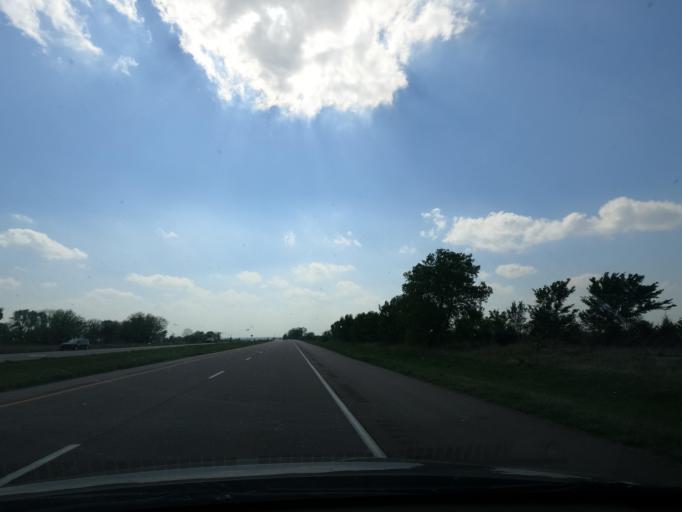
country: US
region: Kansas
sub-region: Butler County
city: Towanda
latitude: 37.8123
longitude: -96.9542
